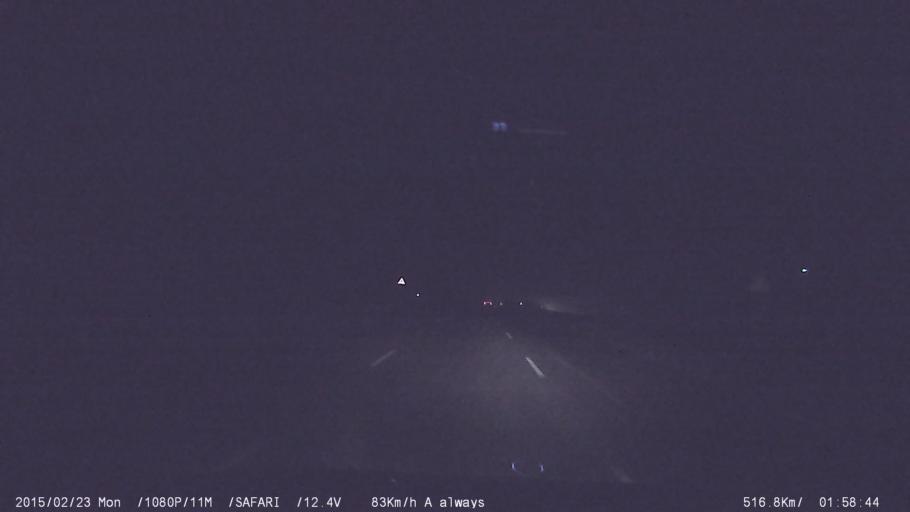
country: IN
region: Tamil Nadu
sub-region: Krishnagiri
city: Krishnagiri
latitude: 12.6087
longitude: 78.0963
